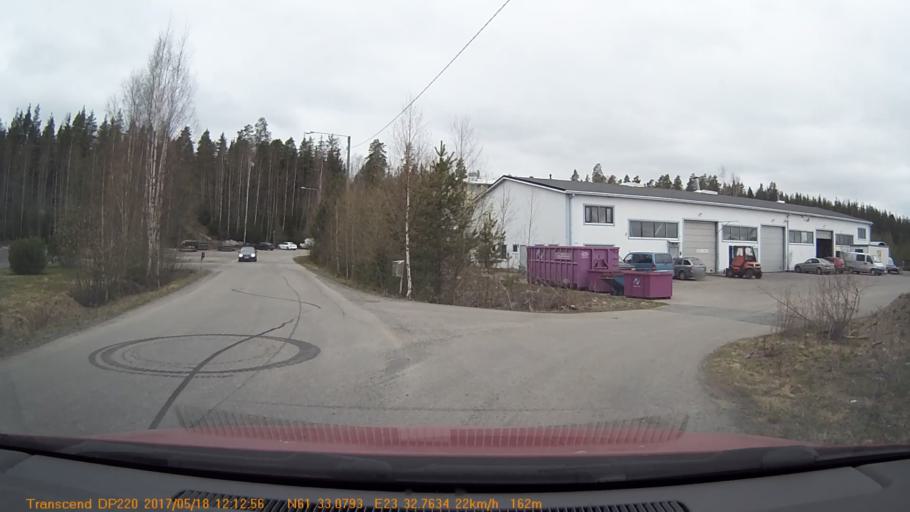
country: FI
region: Pirkanmaa
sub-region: Tampere
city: Yloejaervi
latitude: 61.5511
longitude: 23.5460
